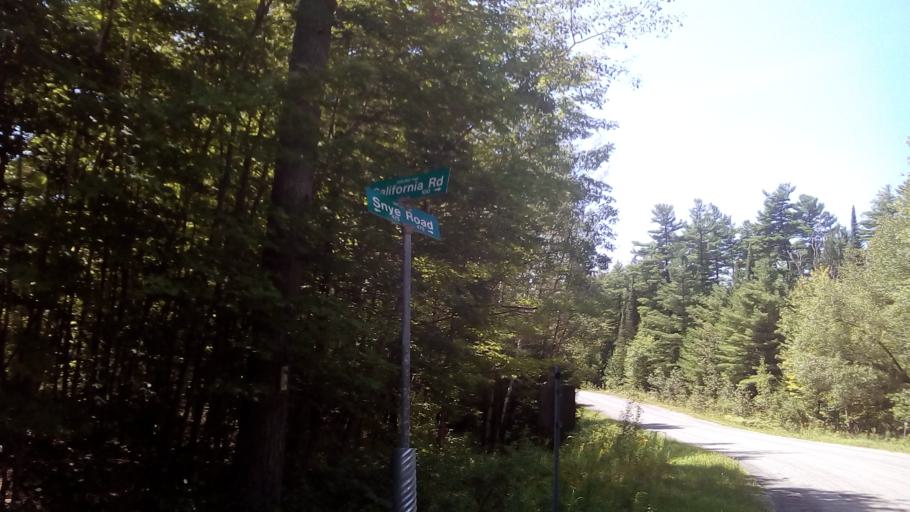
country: CA
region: Ontario
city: Arnprior
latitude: 45.2635
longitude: -76.4792
